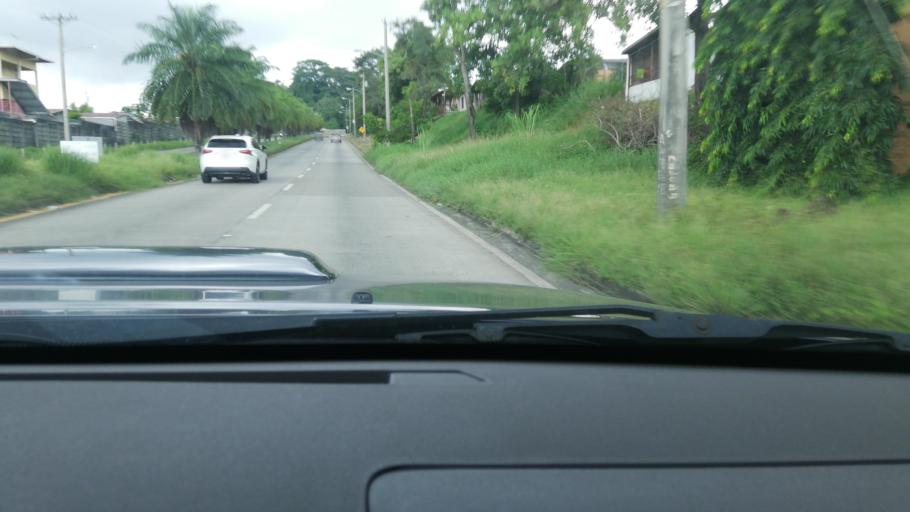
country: PA
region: Panama
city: San Miguelito
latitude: 9.0466
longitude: -79.4834
